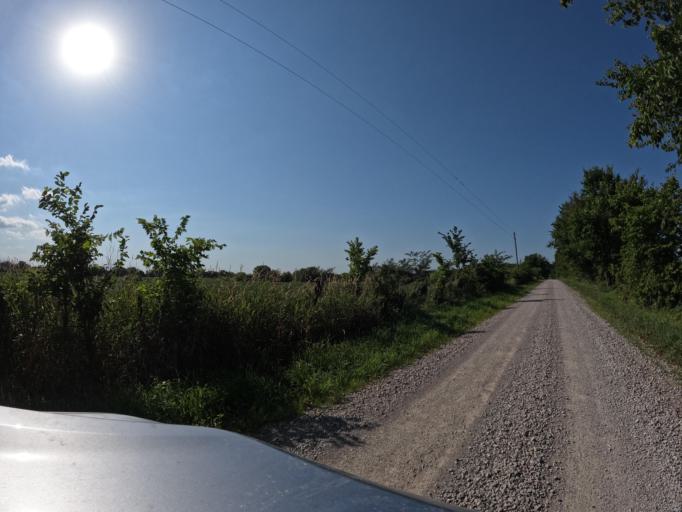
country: US
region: Iowa
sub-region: Appanoose County
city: Centerville
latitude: 40.7269
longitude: -93.0159
